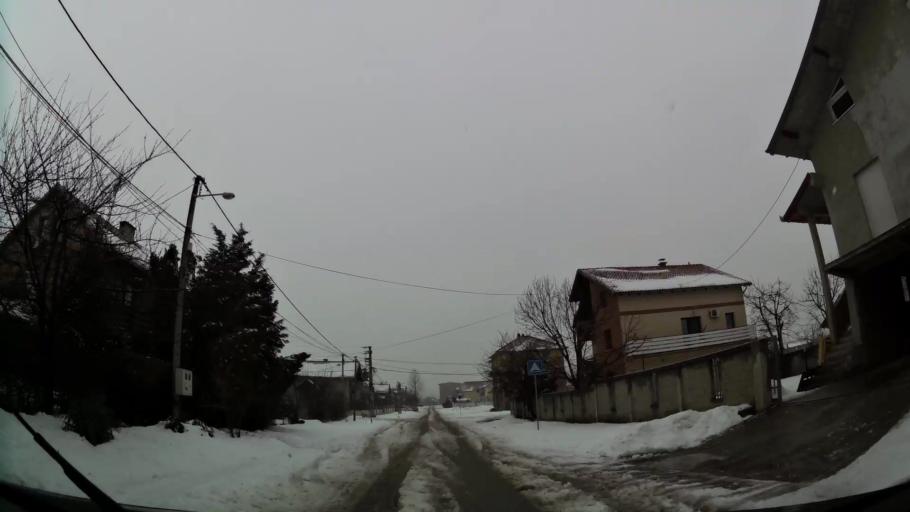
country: RS
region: Central Serbia
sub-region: Belgrade
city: Zemun
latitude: 44.8506
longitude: 20.3418
